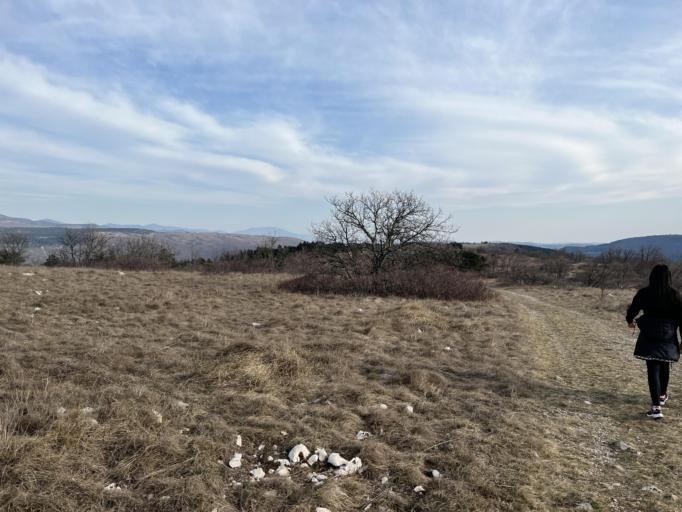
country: SI
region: Koper-Capodistria
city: Sv. Anton
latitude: 45.4793
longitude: 13.8940
